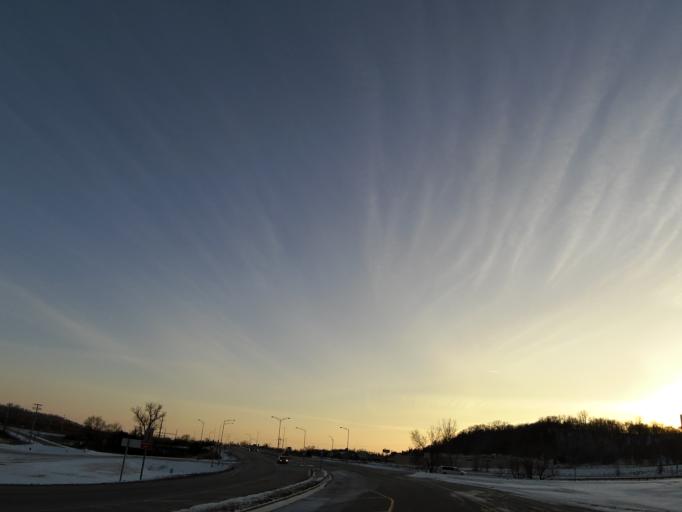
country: US
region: Wisconsin
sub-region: Pierce County
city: River Falls
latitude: 44.8820
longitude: -92.6214
